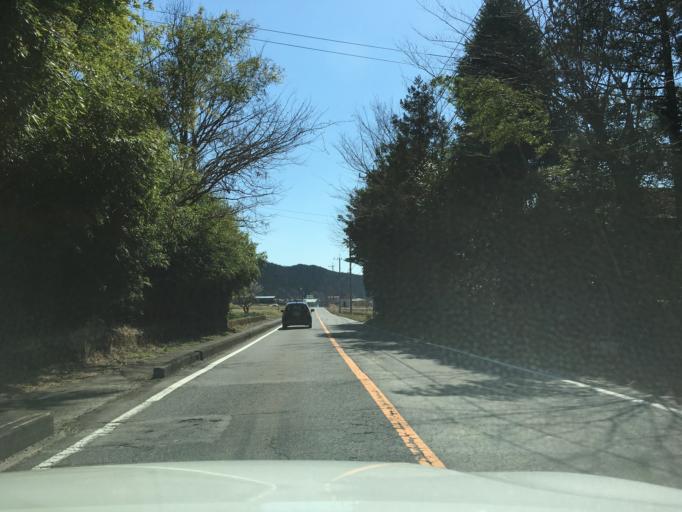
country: JP
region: Tochigi
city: Kuroiso
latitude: 36.9794
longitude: 140.1604
